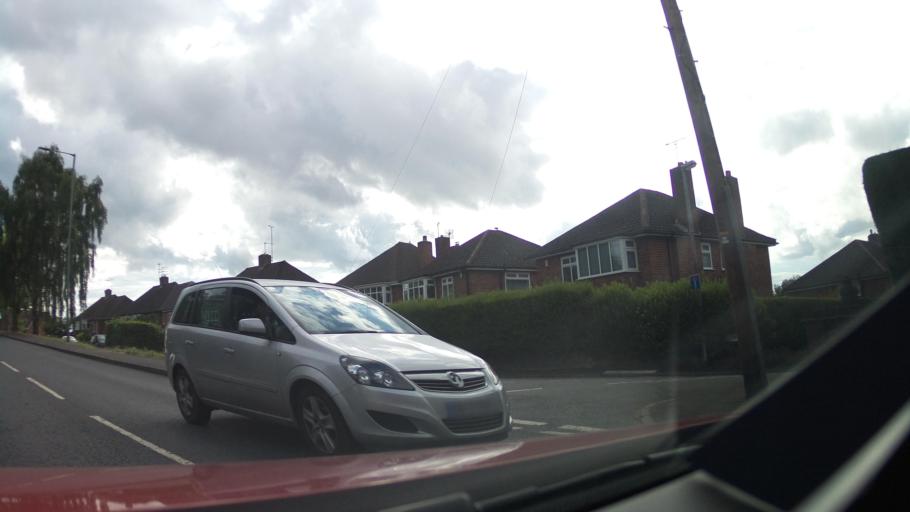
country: GB
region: England
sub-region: Dudley
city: Kingswinford
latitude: 52.5031
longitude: -2.1814
